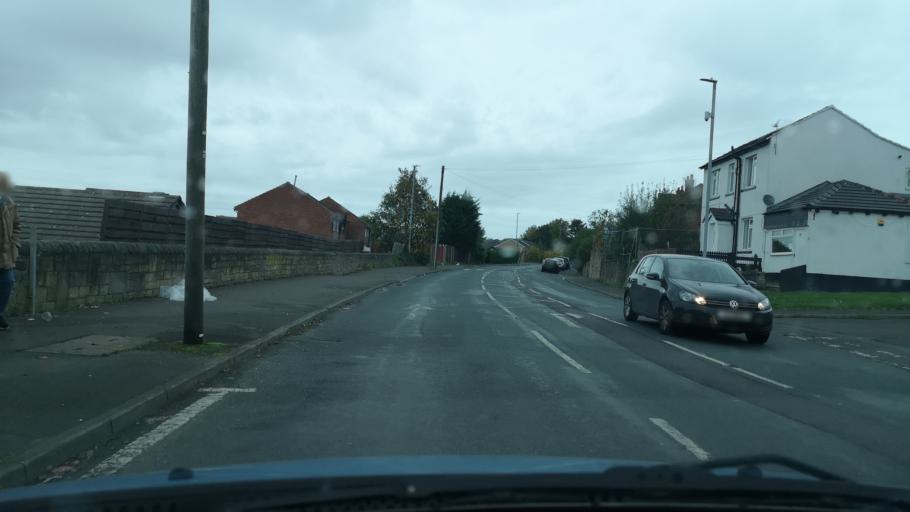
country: GB
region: England
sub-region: Kirklees
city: Heckmondwike
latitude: 53.6894
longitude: -1.6569
